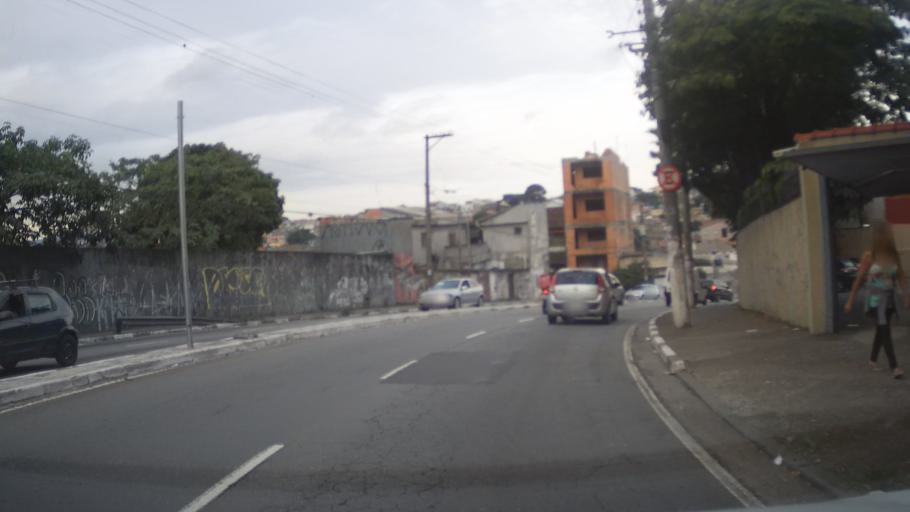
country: BR
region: Sao Paulo
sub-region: Guarulhos
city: Guarulhos
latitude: -23.4511
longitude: -46.5153
